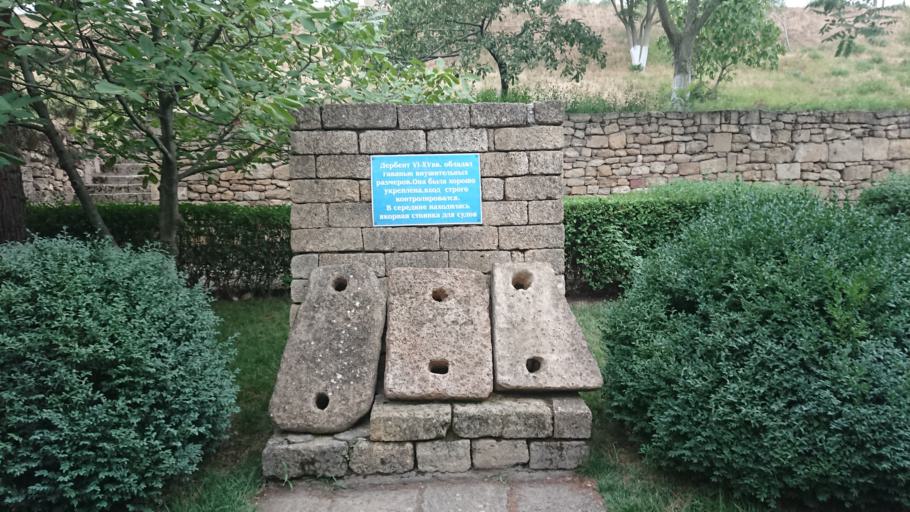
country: RU
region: Dagestan
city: Derbent
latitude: 42.0532
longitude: 48.2746
